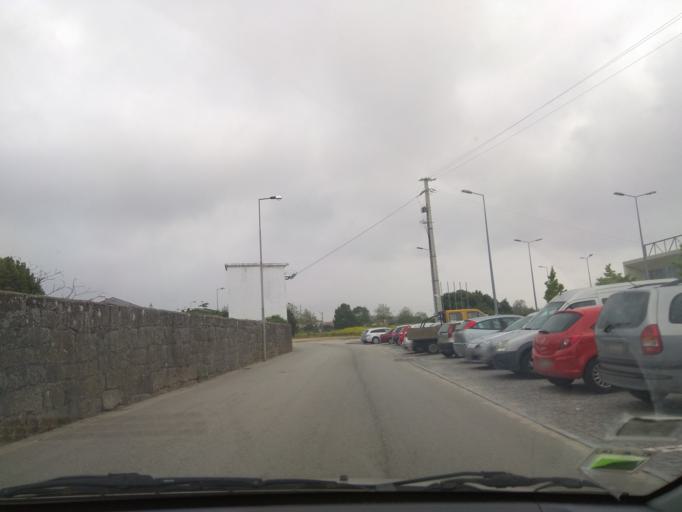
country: PT
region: Porto
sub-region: Matosinhos
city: Guifoes
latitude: 41.1994
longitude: -8.6656
